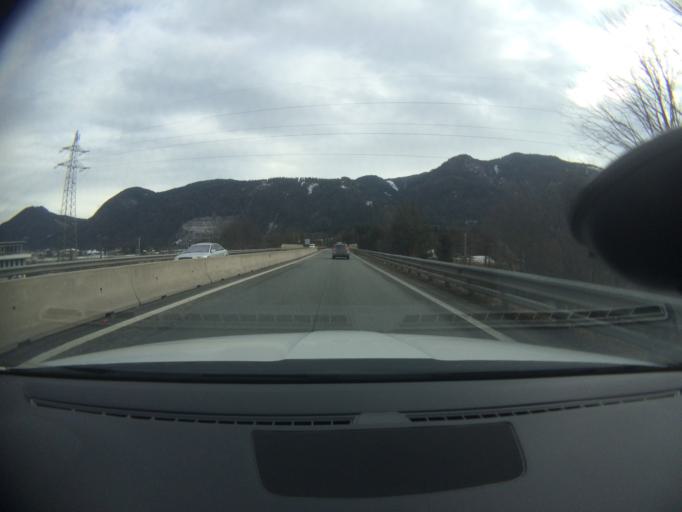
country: AT
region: Tyrol
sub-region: Politischer Bezirk Kufstein
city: Worgl
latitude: 47.4827
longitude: 12.0270
